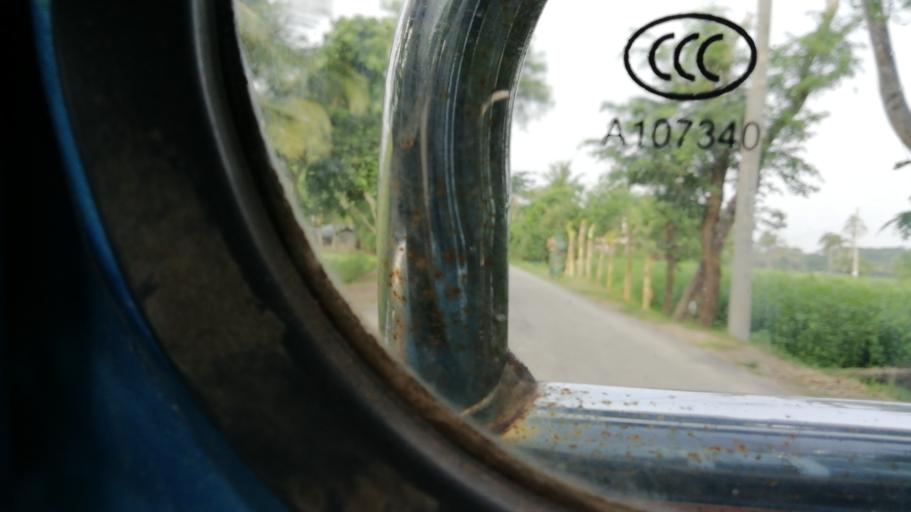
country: BD
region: Khulna
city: Kesabpur
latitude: 23.0342
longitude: 89.2827
